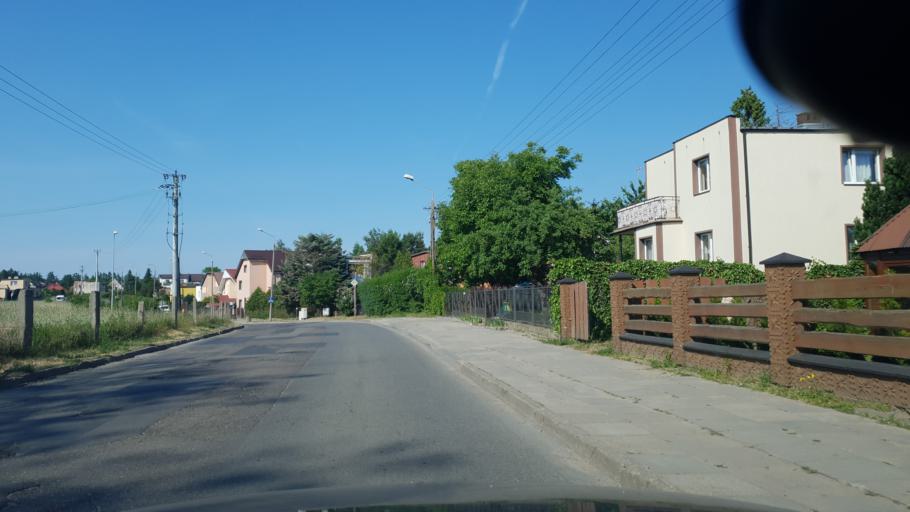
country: PL
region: Pomeranian Voivodeship
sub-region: Powiat kartuski
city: Chwaszczyno
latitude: 54.4273
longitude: 18.4603
